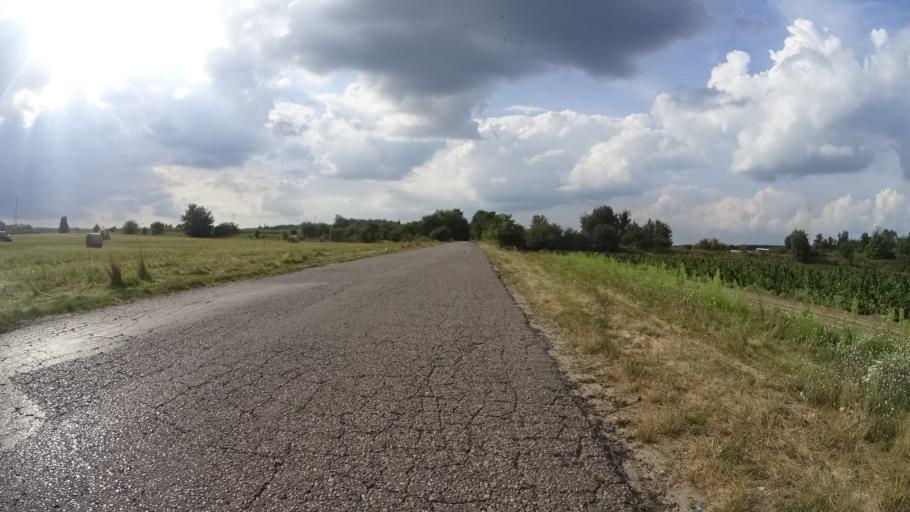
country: PL
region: Masovian Voivodeship
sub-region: Powiat grojecki
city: Mogielnica
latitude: 51.6656
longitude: 20.7428
